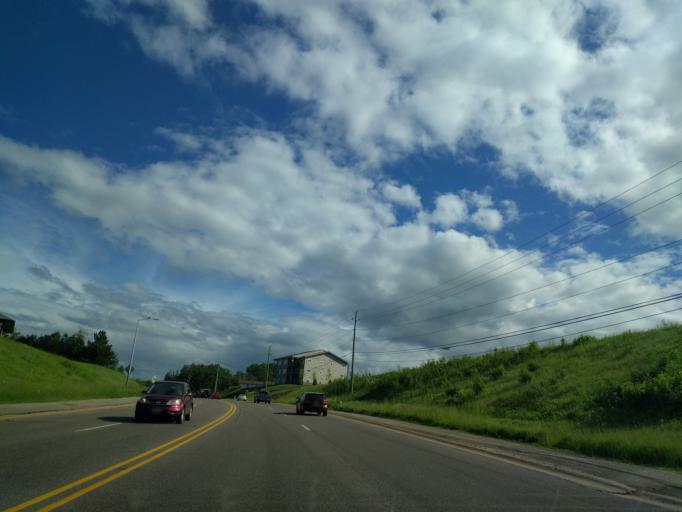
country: US
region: Michigan
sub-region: Marquette County
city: Trowbridge Park
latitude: 46.5424
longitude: -87.4199
